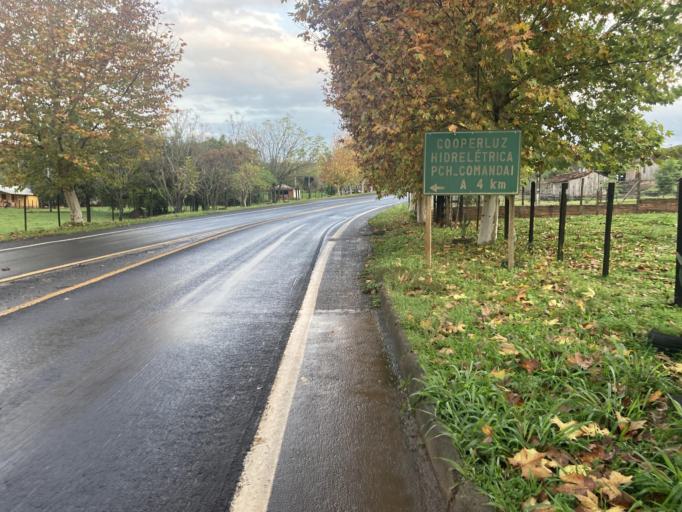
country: BR
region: Rio Grande do Sul
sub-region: Sao Pedro Do Butia
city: Butia Inferior
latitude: -27.9911
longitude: -54.8324
